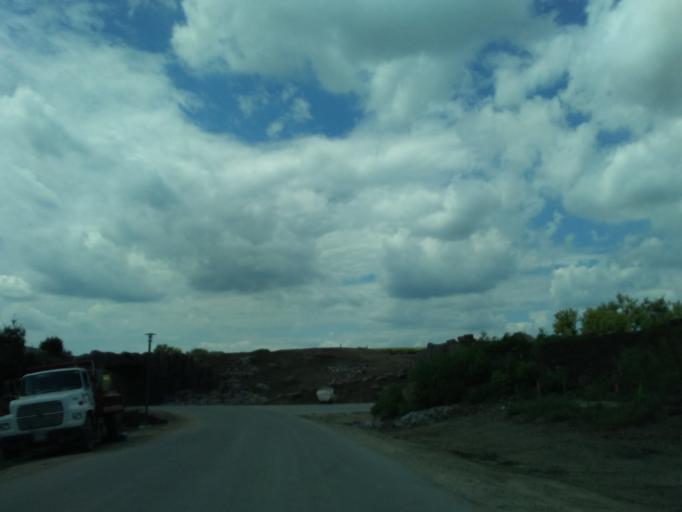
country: US
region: Wisconsin
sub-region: Dane County
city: Verona
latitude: 43.0003
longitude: -89.5668
